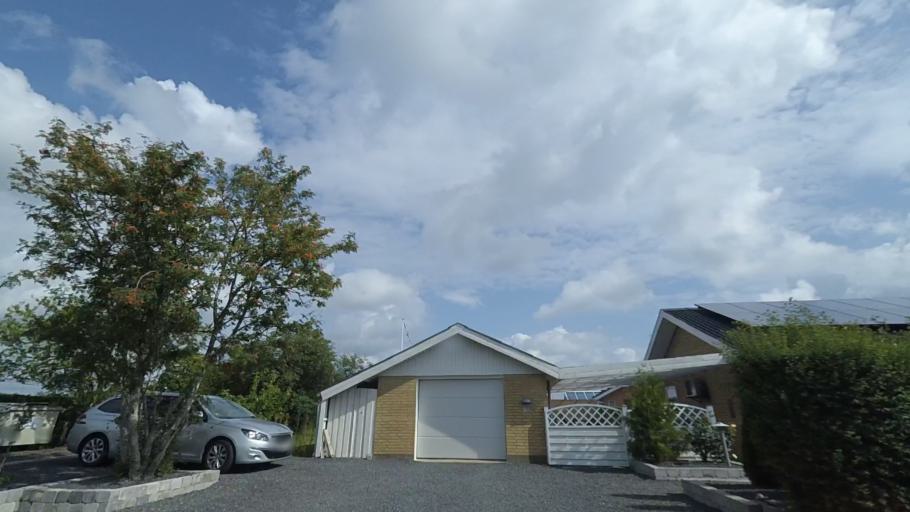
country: DK
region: Central Jutland
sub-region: Syddjurs Kommune
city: Ryomgard
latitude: 56.4796
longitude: 10.5055
